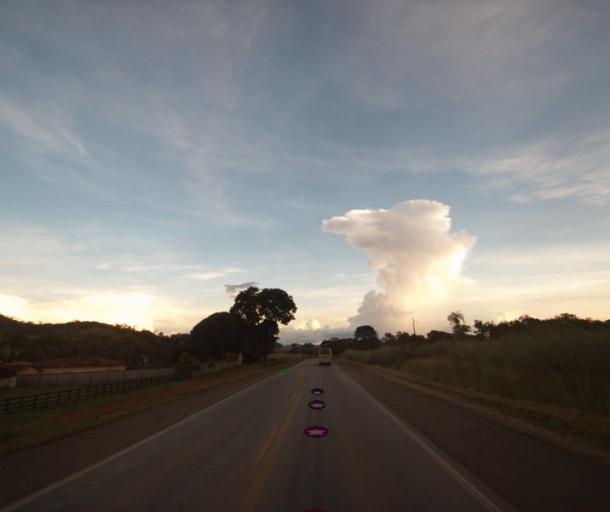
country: BR
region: Goias
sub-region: Uruacu
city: Uruacu
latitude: -14.4018
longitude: -49.1576
